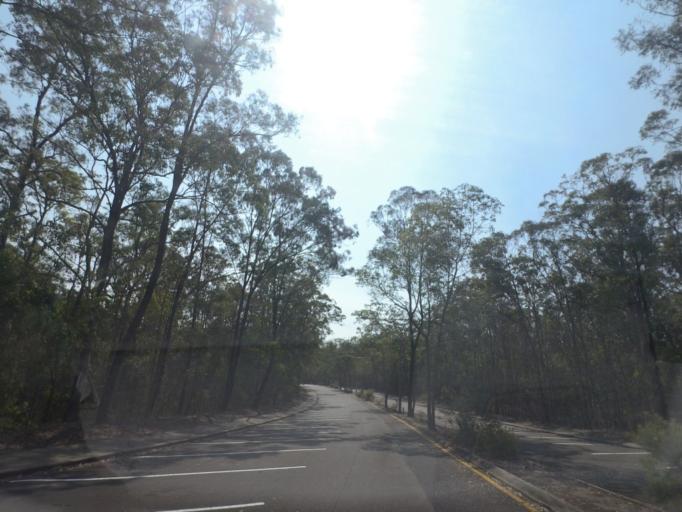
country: AU
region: Queensland
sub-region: Brisbane
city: Nathan
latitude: -27.5489
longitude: 153.0521
